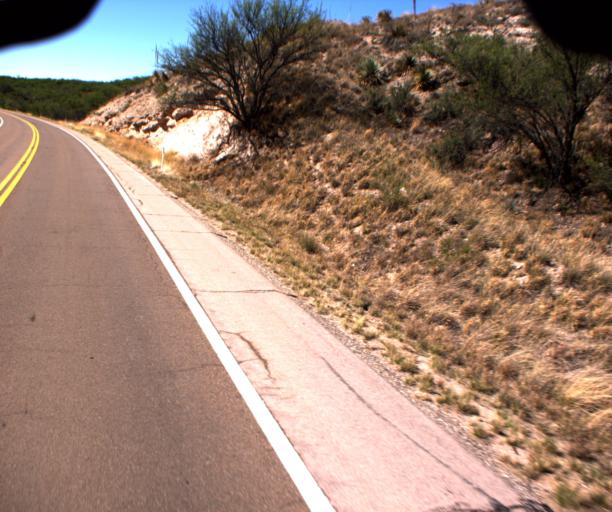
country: US
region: Arizona
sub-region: Santa Cruz County
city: Rio Rico
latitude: 31.6503
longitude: -110.7154
